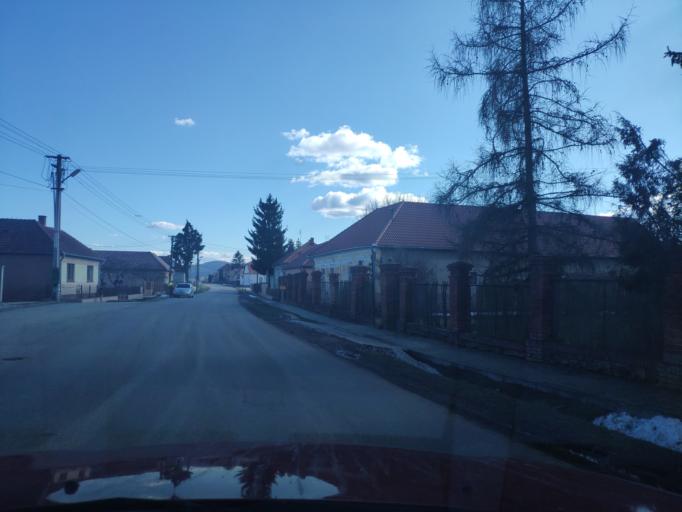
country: SK
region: Banskobystricky
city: Rimavska Sobota
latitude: 48.2915
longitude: 20.0848
